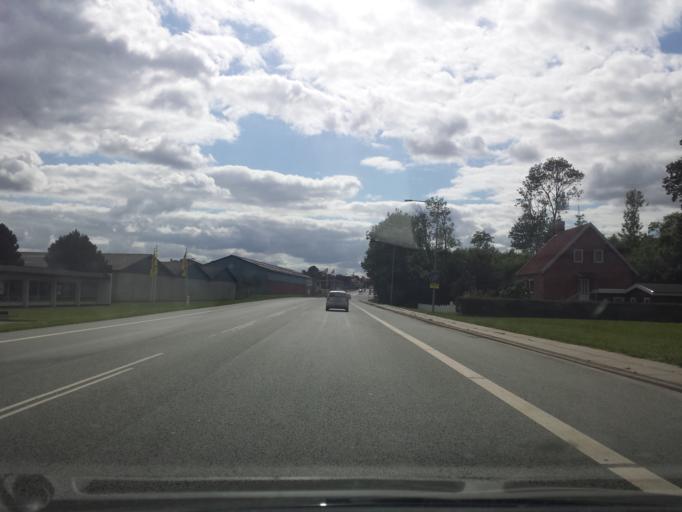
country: DK
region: South Denmark
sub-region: Sonderborg Kommune
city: Sonderborg
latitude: 54.9207
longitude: 9.8143
